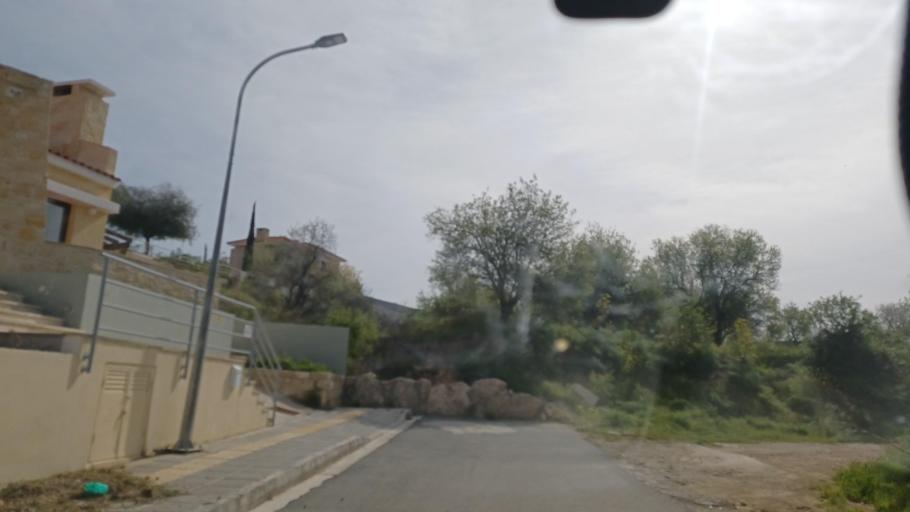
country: CY
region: Pafos
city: Mesogi
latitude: 34.7830
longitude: 32.4683
